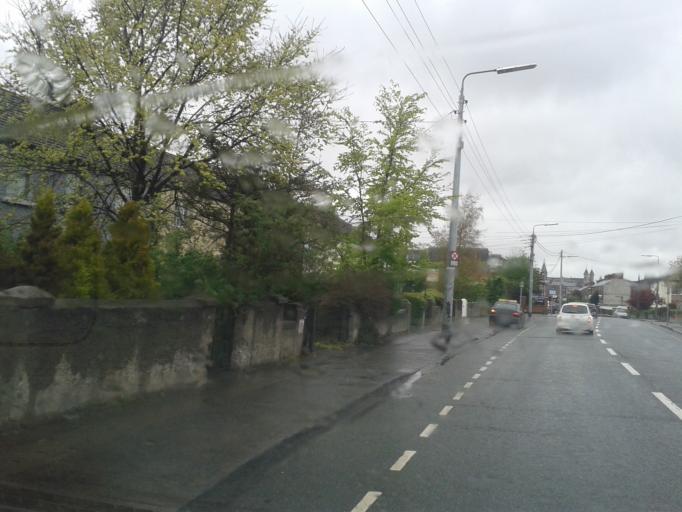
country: IE
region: Leinster
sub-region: South Dublin
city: Terenure
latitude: 53.3169
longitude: -6.2938
